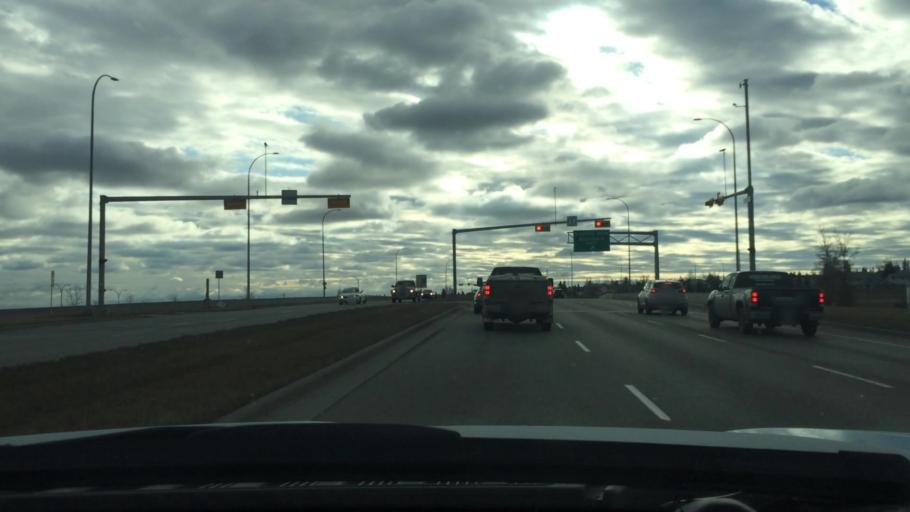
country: CA
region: Alberta
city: Calgary
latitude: 51.1452
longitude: -114.0940
